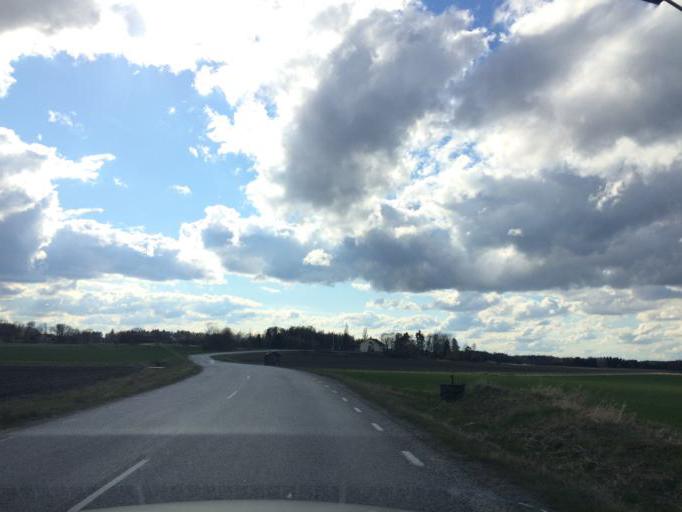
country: SE
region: Soedermanland
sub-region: Eskilstuna Kommun
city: Eskilstuna
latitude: 59.4162
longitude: 16.5651
